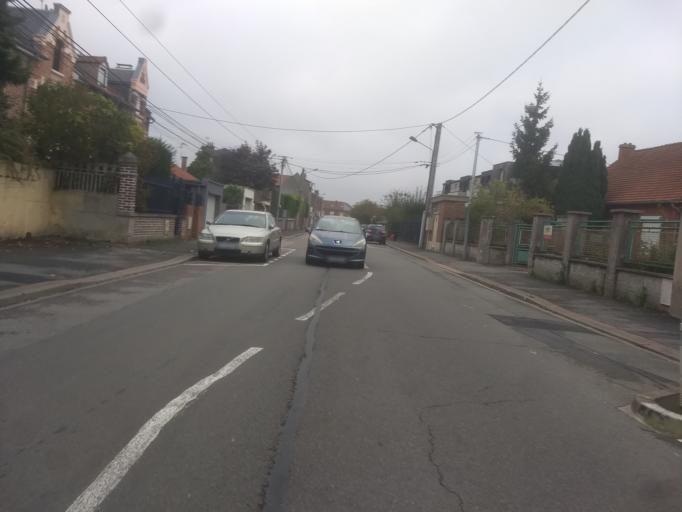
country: FR
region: Nord-Pas-de-Calais
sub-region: Departement du Pas-de-Calais
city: Arras
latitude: 50.2875
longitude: 2.7936
